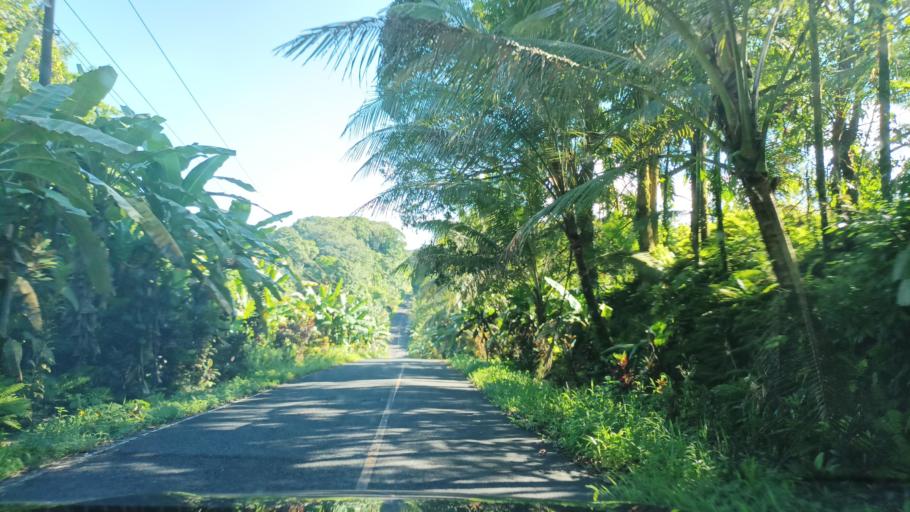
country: FM
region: Pohnpei
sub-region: Madolenihm Municipality
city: Madolenihm Municipality Government
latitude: 6.8159
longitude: 158.2955
